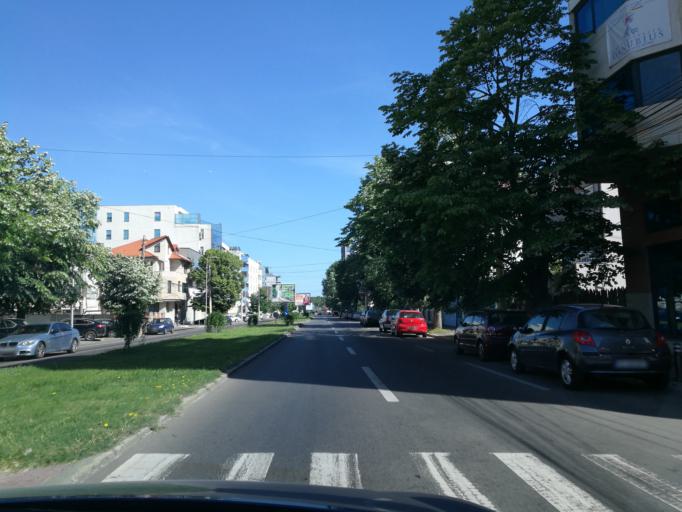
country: RO
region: Constanta
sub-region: Municipiul Constanta
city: Constanta
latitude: 44.2019
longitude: 28.6458
